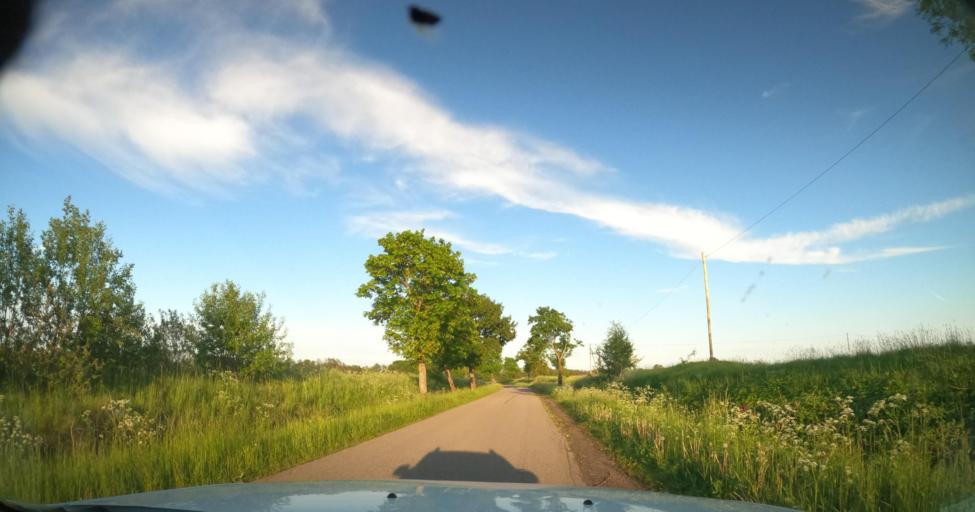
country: PL
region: Warmian-Masurian Voivodeship
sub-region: Powiat lidzbarski
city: Orneta
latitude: 54.1718
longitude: 20.1670
